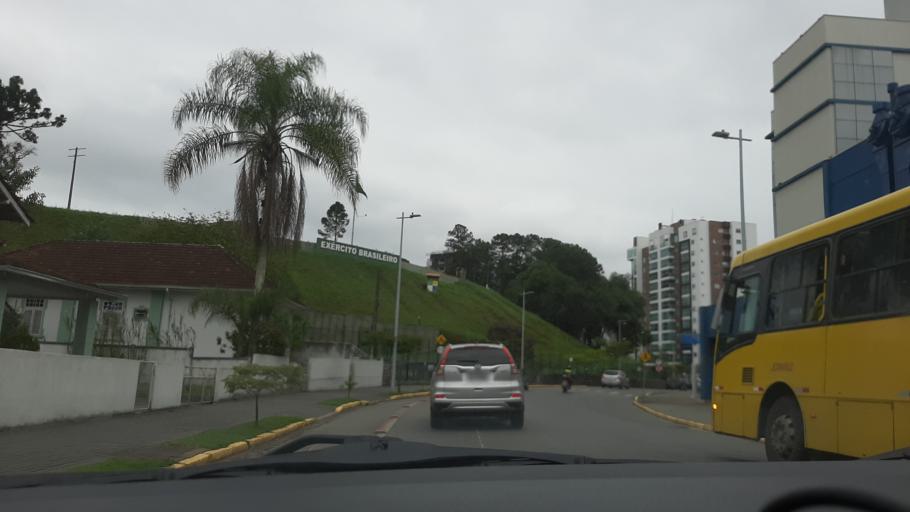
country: BR
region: Santa Catarina
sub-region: Joinville
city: Joinville
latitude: -26.3061
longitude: -48.8532
